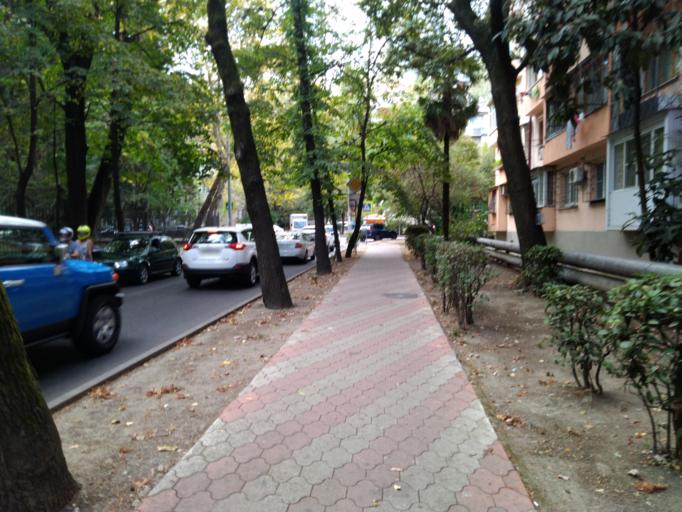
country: RU
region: Krasnodarskiy
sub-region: Sochi City
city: Sochi
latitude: 43.6026
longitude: 39.7229
